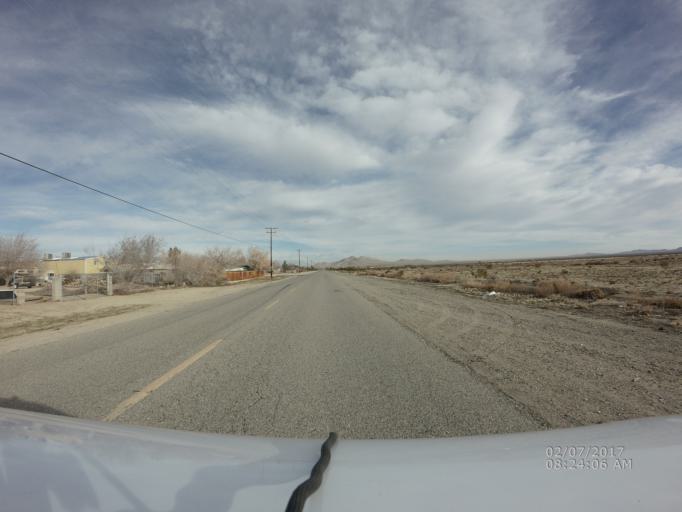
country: US
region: California
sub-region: Los Angeles County
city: Lake Los Angeles
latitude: 34.6049
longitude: -117.8093
